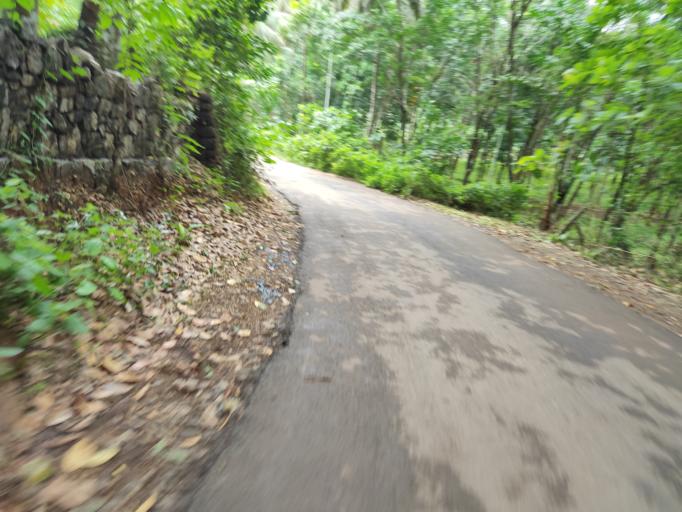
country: IN
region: Kerala
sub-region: Malappuram
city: Manjeri
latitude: 11.2215
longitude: 76.2527
